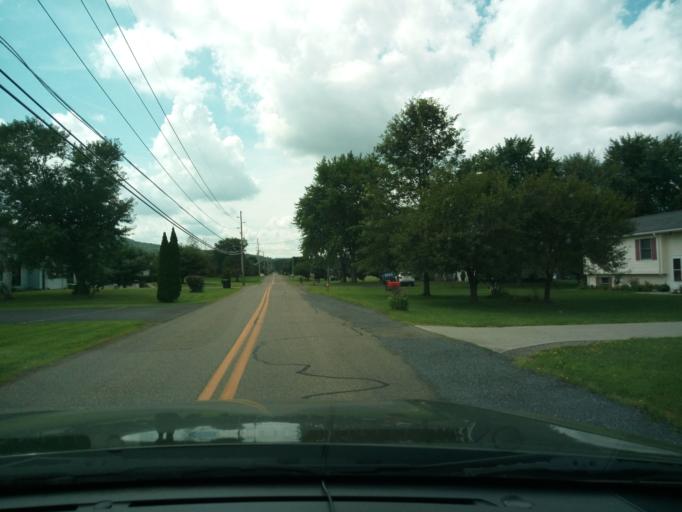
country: US
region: Pennsylvania
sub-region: Bradford County
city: South Waverly
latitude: 41.9959
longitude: -76.5672
